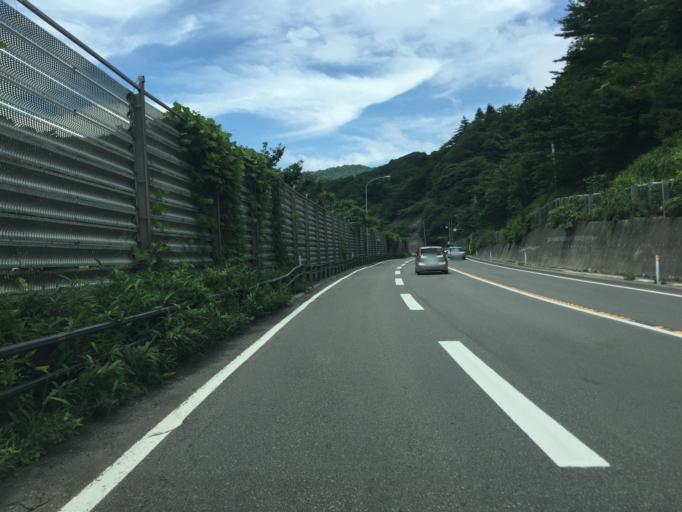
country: JP
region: Fukushima
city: Fukushima-shi
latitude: 37.8405
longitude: 140.3056
